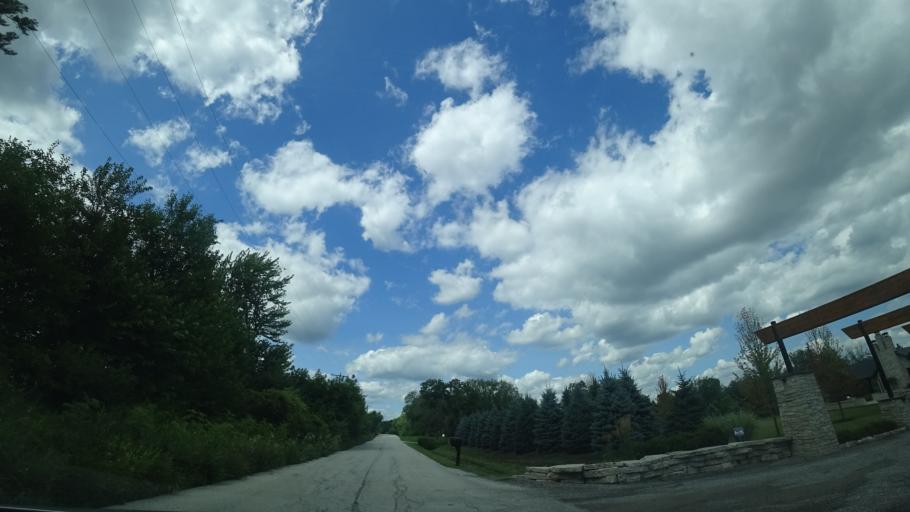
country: US
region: Illinois
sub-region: Will County
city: Homer Glen
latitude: 41.5953
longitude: -87.9058
